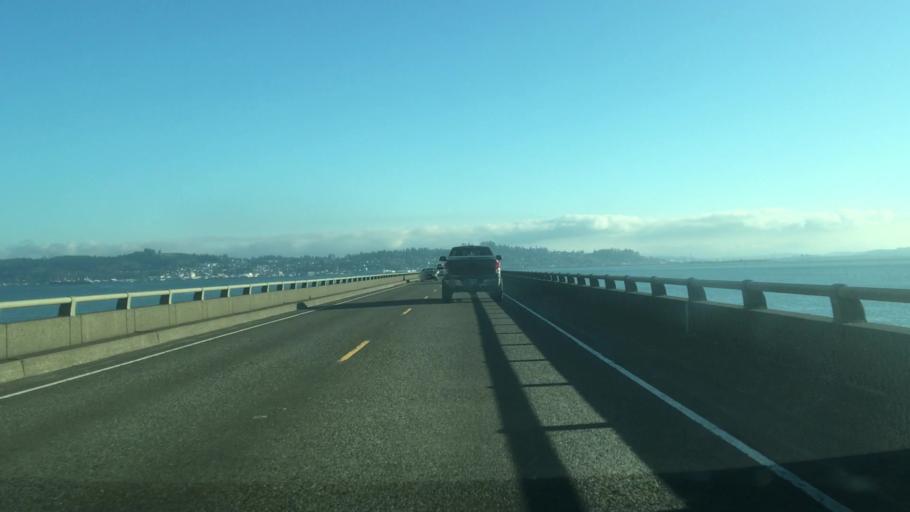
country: US
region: Oregon
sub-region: Clatsop County
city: Astoria
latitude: 46.2256
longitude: -123.8672
